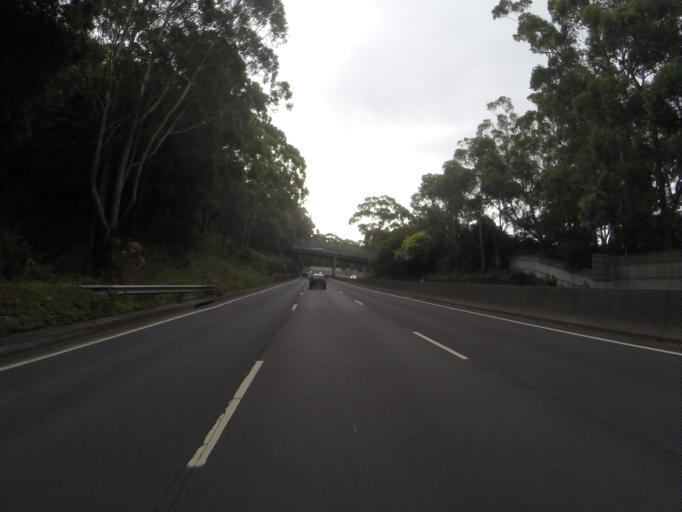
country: AU
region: New South Wales
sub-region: Wollongong
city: Mount Ousley
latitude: -34.3970
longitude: 150.8677
